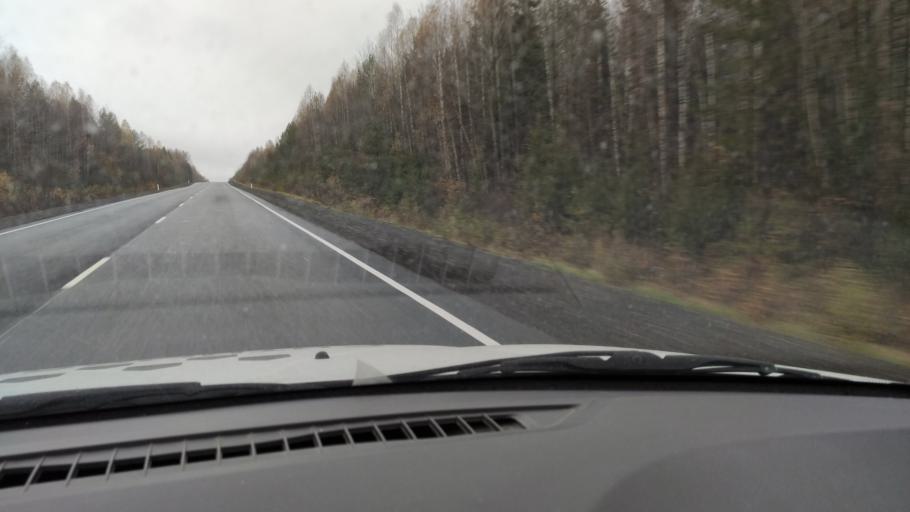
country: RU
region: Kirov
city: Chernaya Kholunitsa
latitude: 58.8805
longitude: 51.4403
